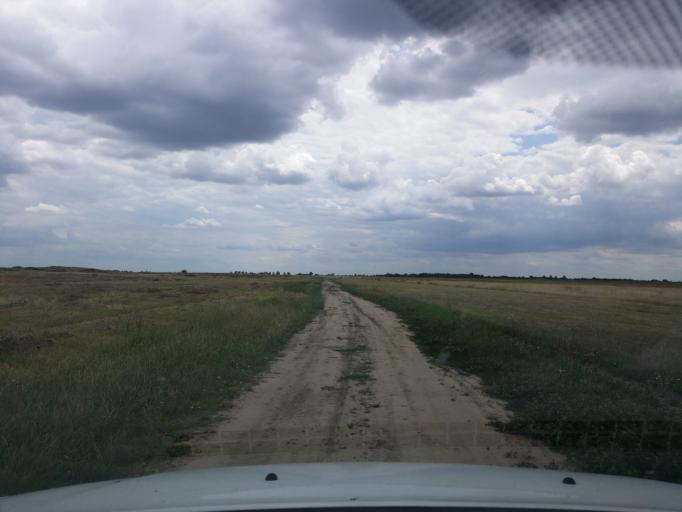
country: HU
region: Hajdu-Bihar
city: Egyek
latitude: 47.5695
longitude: 20.9448
